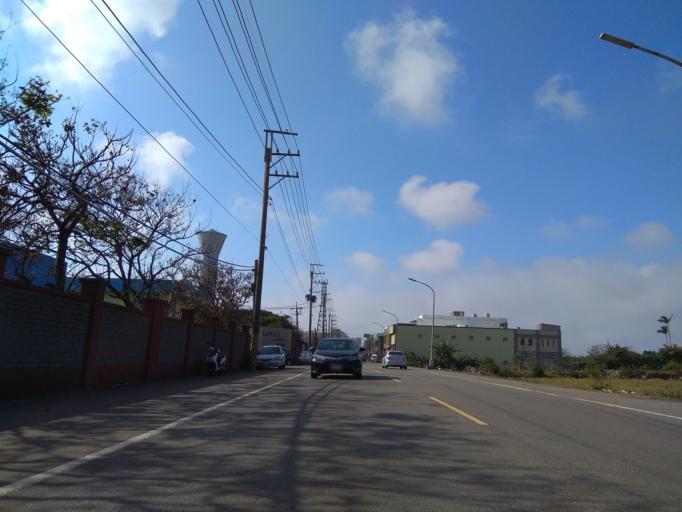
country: TW
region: Taiwan
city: Taoyuan City
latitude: 25.0343
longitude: 121.0896
